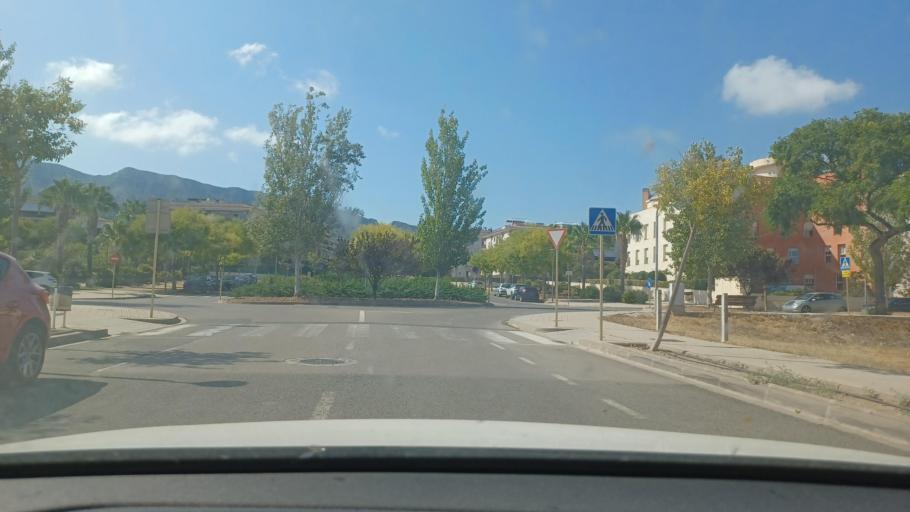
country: ES
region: Catalonia
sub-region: Provincia de Tarragona
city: Sant Carles de la Rapita
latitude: 40.6086
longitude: 0.5824
